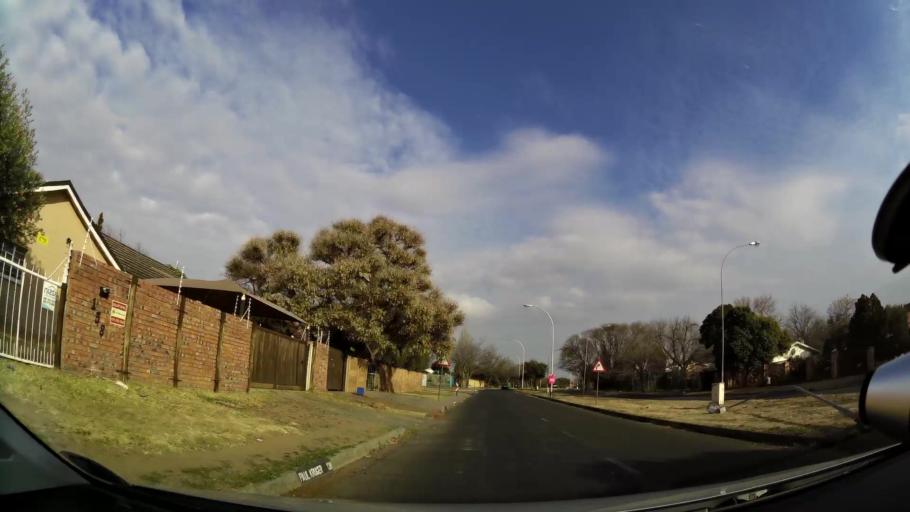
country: ZA
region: Orange Free State
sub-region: Mangaung Metropolitan Municipality
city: Bloemfontein
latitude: -29.1238
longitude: 26.1775
